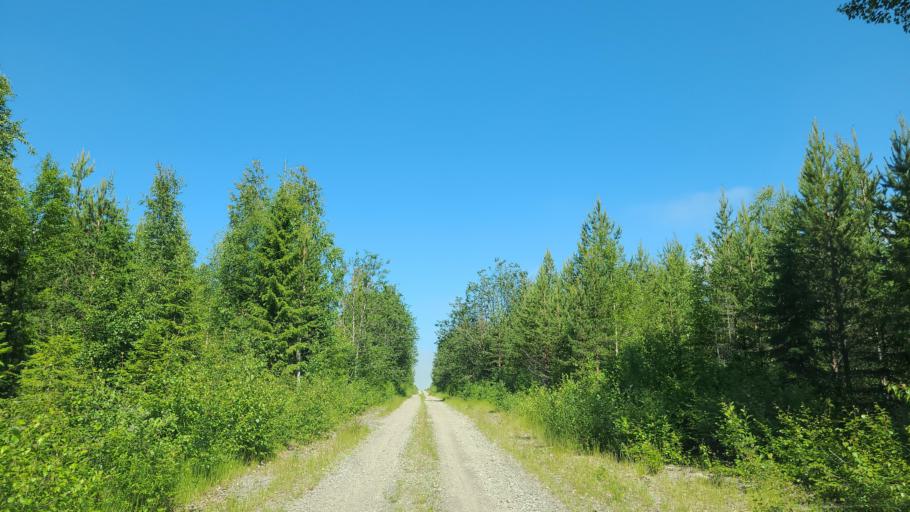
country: SE
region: Vaesternorrland
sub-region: OErnskoeldsviks Kommun
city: Husum
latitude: 63.4359
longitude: 19.2312
